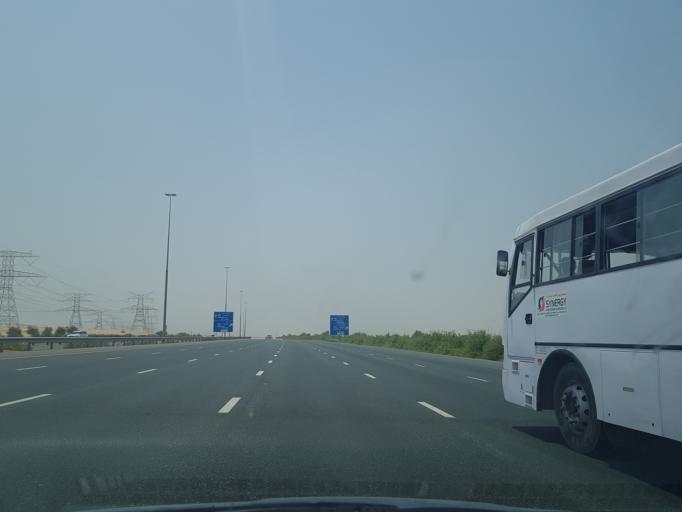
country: AE
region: Dubai
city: Dubai
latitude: 25.0642
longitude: 55.3328
